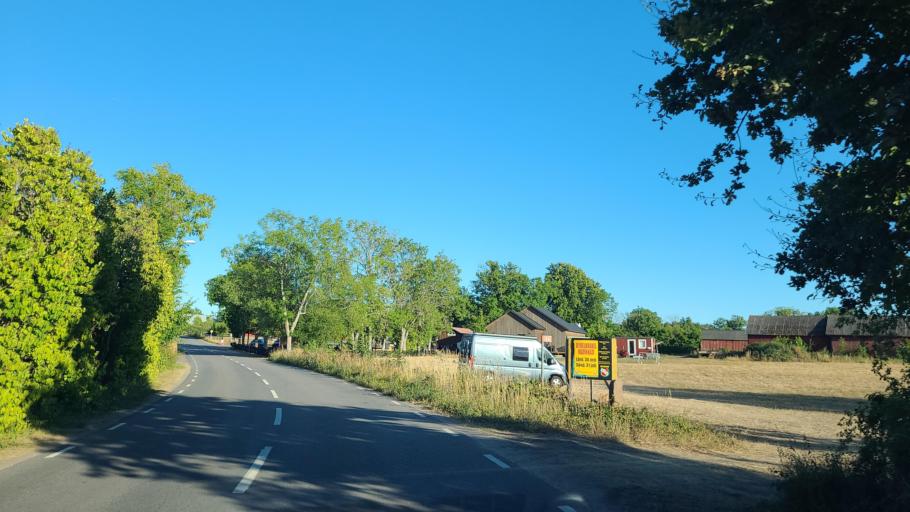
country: SE
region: Kalmar
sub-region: Oskarshamns Kommun
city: Oskarshamn
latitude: 57.3234
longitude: 17.0098
